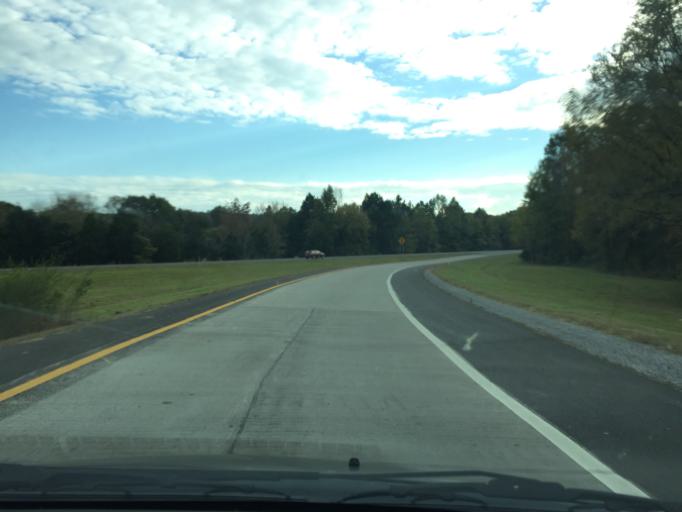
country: US
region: Tennessee
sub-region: Monroe County
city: Sweetwater
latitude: 35.6221
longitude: -84.4941
